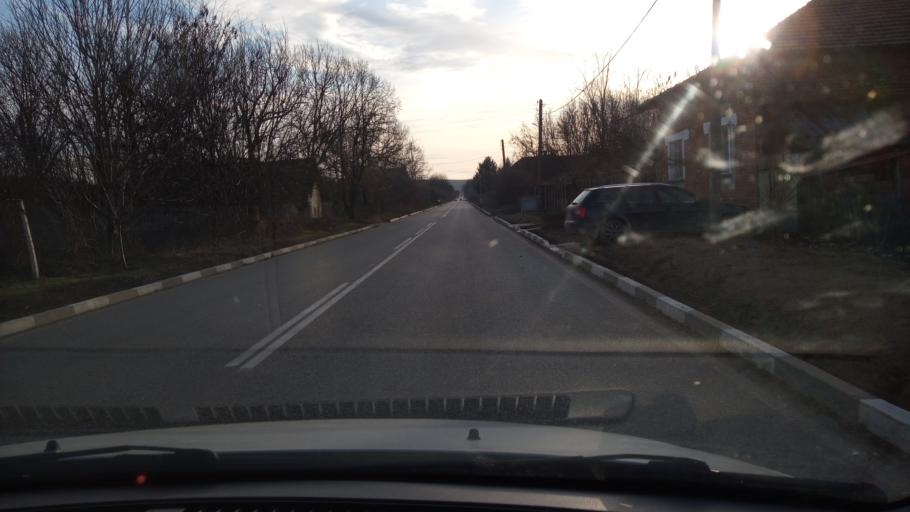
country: BG
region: Pleven
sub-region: Obshtina Pleven
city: Slavyanovo
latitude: 43.5600
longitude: 24.8685
